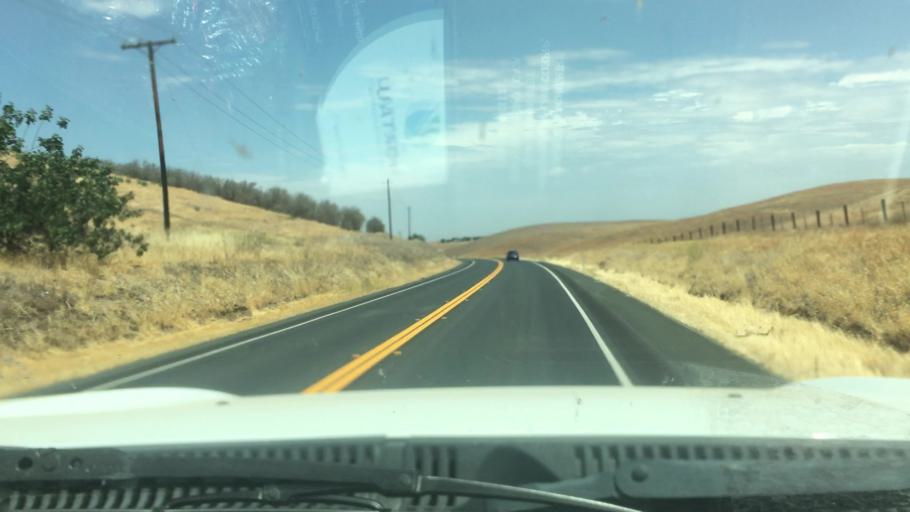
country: US
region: California
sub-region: Tulare County
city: Richgrove
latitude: 35.6993
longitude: -119.0629
